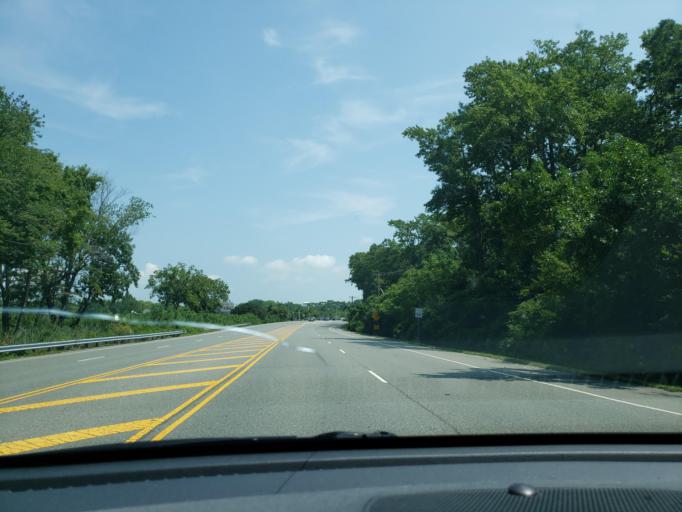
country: US
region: New Jersey
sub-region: Cape May County
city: North Cape May
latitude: 38.9734
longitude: -74.9387
